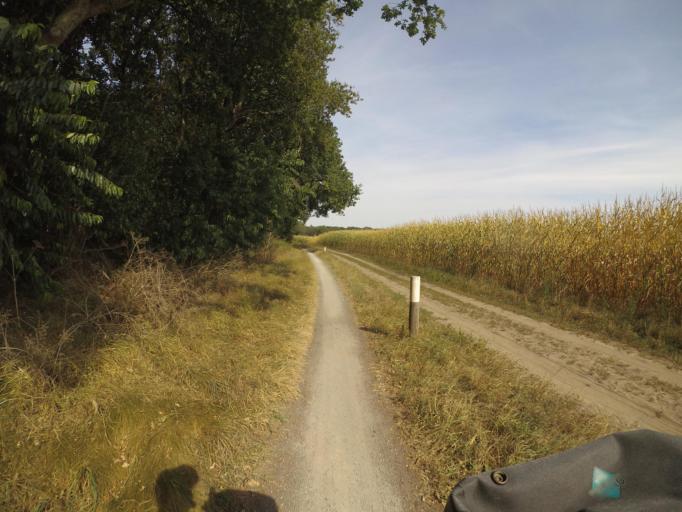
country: NL
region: Drenthe
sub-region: Gemeente Westerveld
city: Havelte
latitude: 52.7834
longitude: 6.2135
